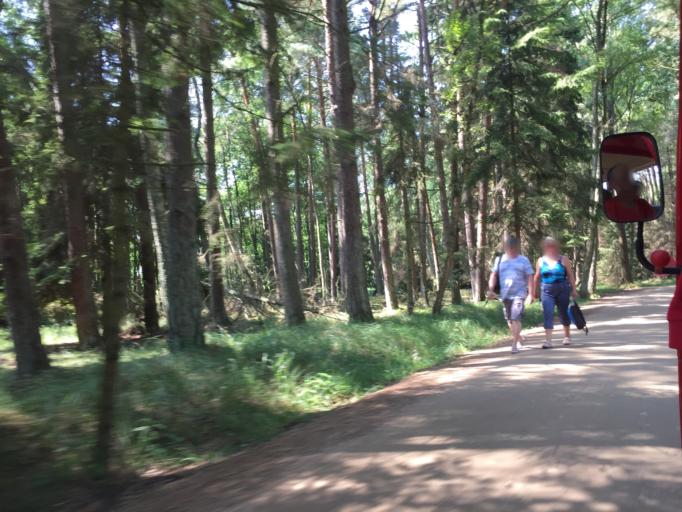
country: PL
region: Pomeranian Voivodeship
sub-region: Powiat leborski
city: Leba
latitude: 54.7485
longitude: 17.4552
